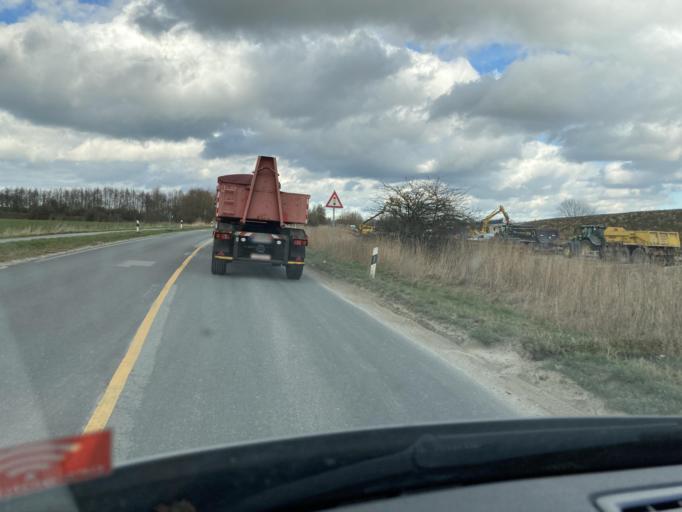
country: DE
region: Lower Saxony
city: Sande
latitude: 53.5177
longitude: 8.0228
